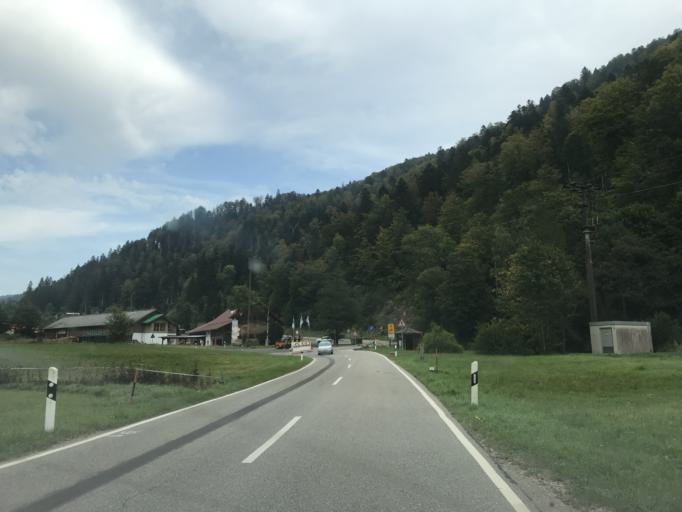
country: DE
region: Baden-Wuerttemberg
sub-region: Freiburg Region
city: Herrischried
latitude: 47.6998
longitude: 7.9847
